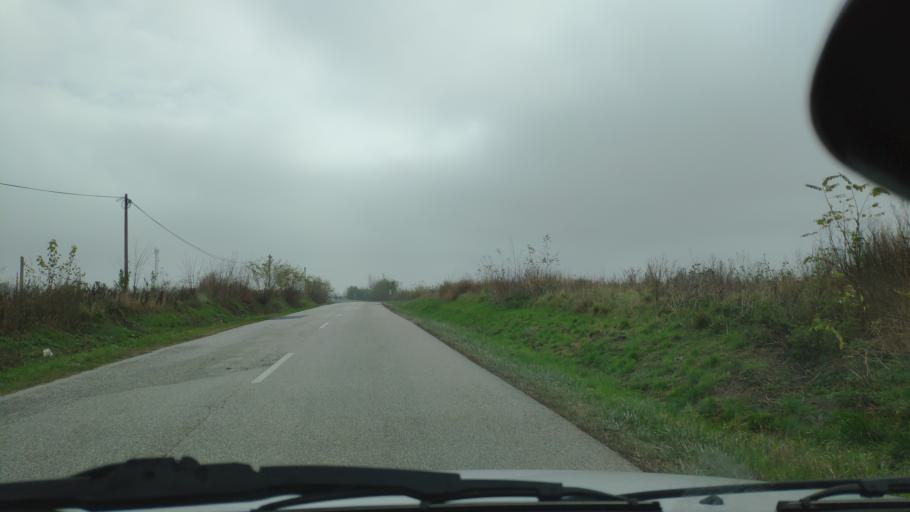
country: HU
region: Somogy
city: Balatonbereny
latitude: 46.6536
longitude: 17.2973
